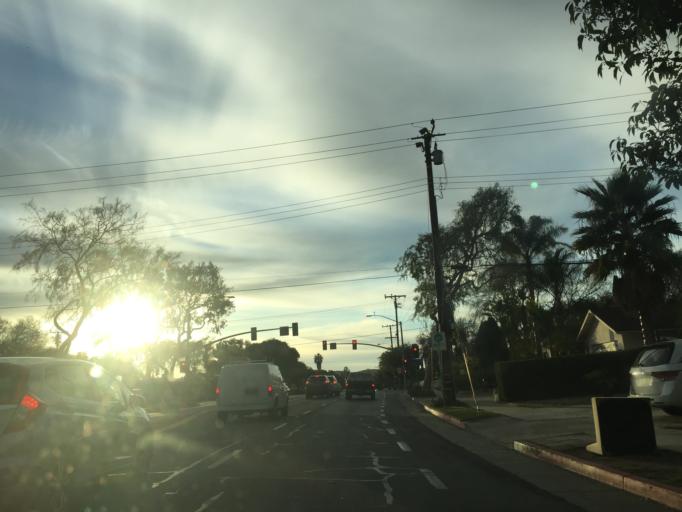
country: US
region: California
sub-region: Santa Barbara County
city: Goleta
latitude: 34.4515
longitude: -119.8196
